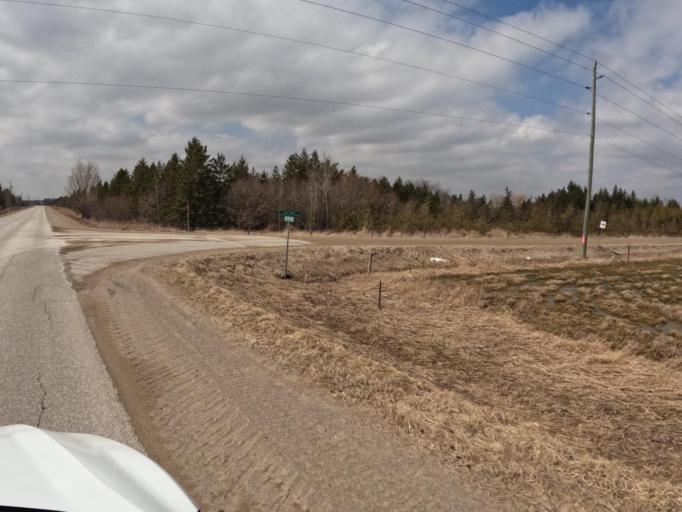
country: CA
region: Ontario
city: Shelburne
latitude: 44.0169
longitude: -80.1732
